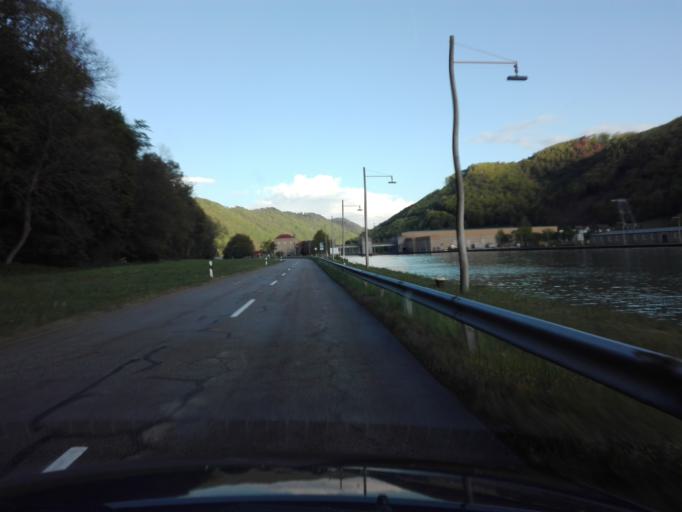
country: DE
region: Bavaria
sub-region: Lower Bavaria
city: Untergriesbach
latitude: 48.5222
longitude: 13.7028
